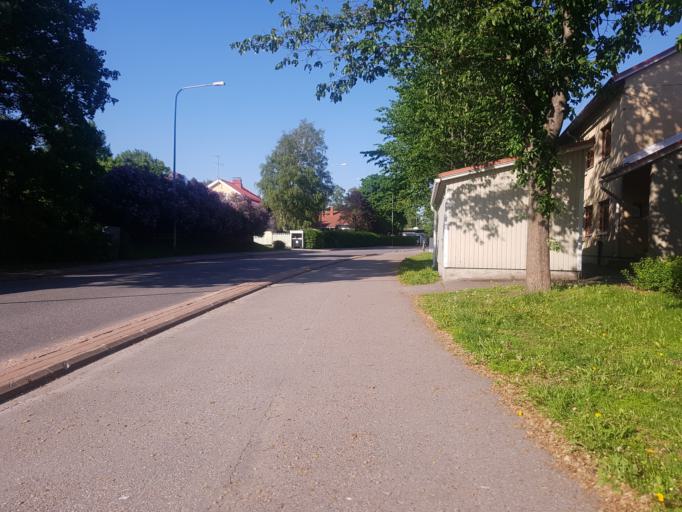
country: FI
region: Uusimaa
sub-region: Helsinki
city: Vantaa
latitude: 60.2598
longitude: 24.9941
